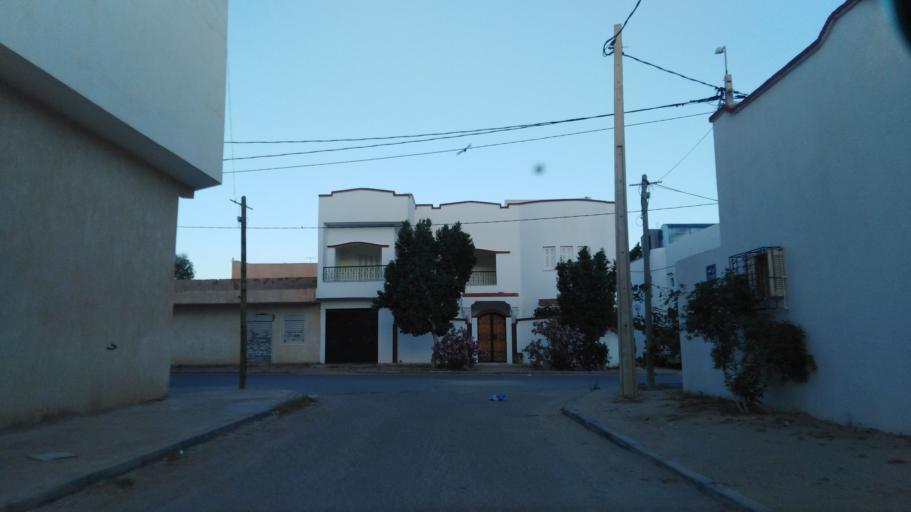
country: TN
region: Tataouine
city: Tataouine
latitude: 32.9413
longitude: 10.4559
